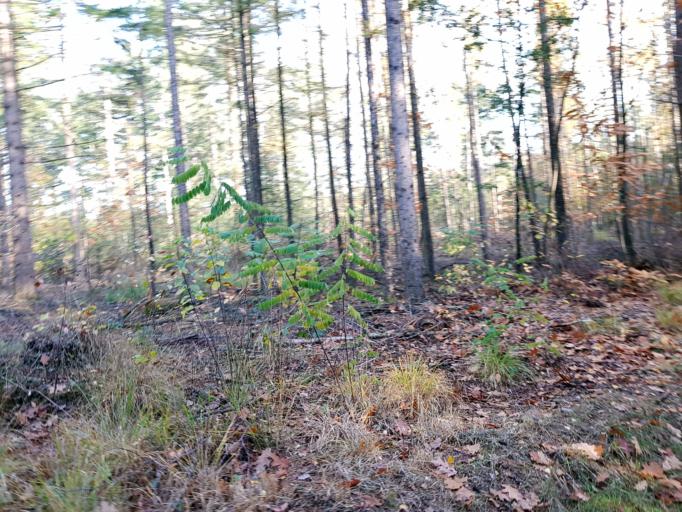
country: NL
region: Gelderland
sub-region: Gemeente Groesbeek
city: Groesbeek
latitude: 51.7845
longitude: 5.9115
